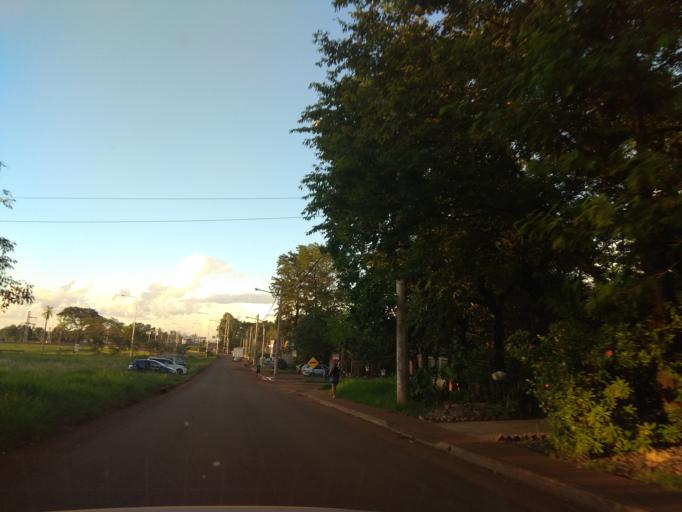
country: AR
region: Misiones
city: Garupa
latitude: -27.4654
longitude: -55.8627
